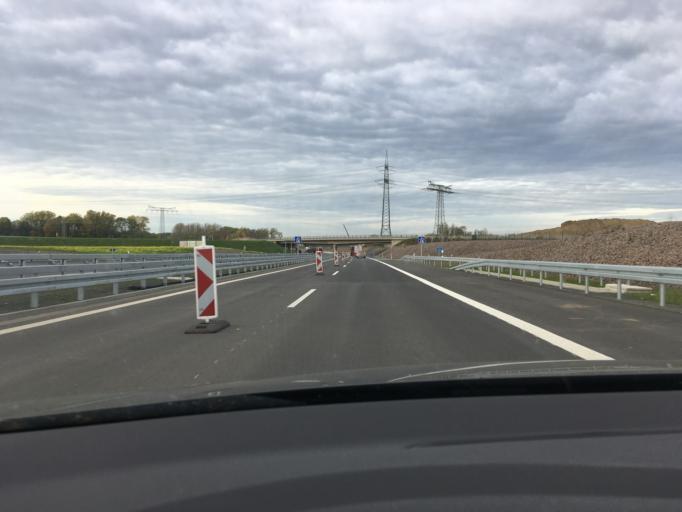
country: DE
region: Saxony
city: Espenhain
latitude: 51.1934
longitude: 12.4443
